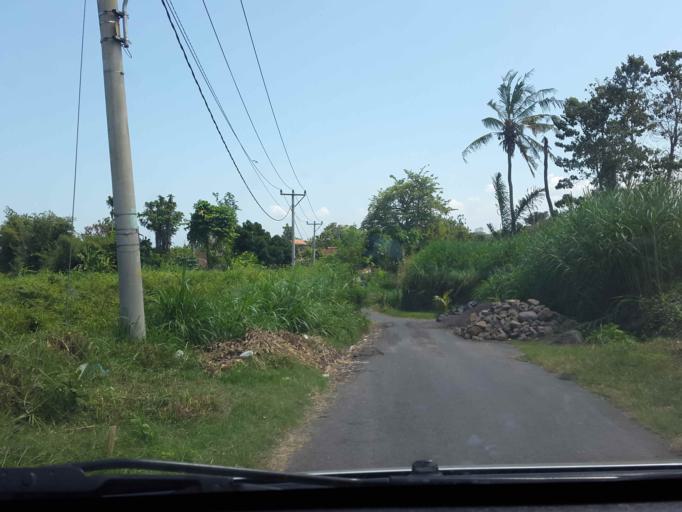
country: ID
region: Bali
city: Semarapura
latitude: -8.5571
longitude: 115.3999
